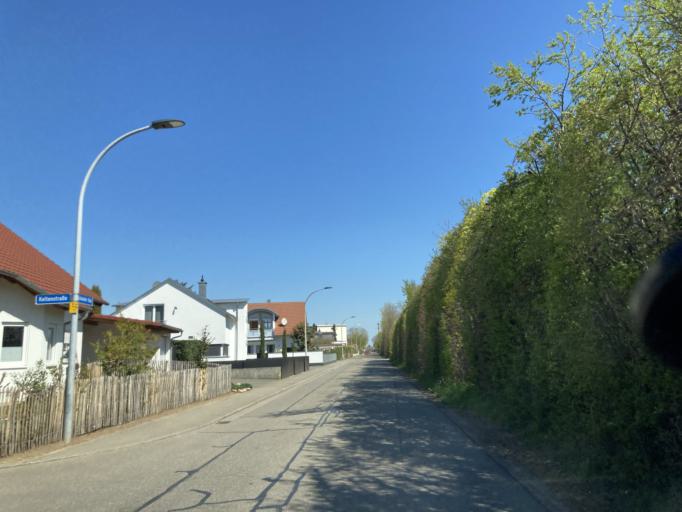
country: DE
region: Baden-Wuerttemberg
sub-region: Freiburg Region
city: Schliengen
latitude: 47.7691
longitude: 7.5568
